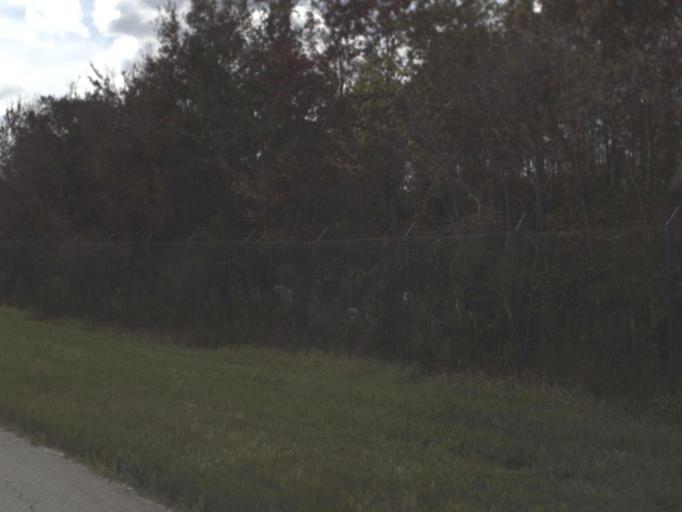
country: US
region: Florida
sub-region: Collier County
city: Immokalee
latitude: 26.1936
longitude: -81.3460
